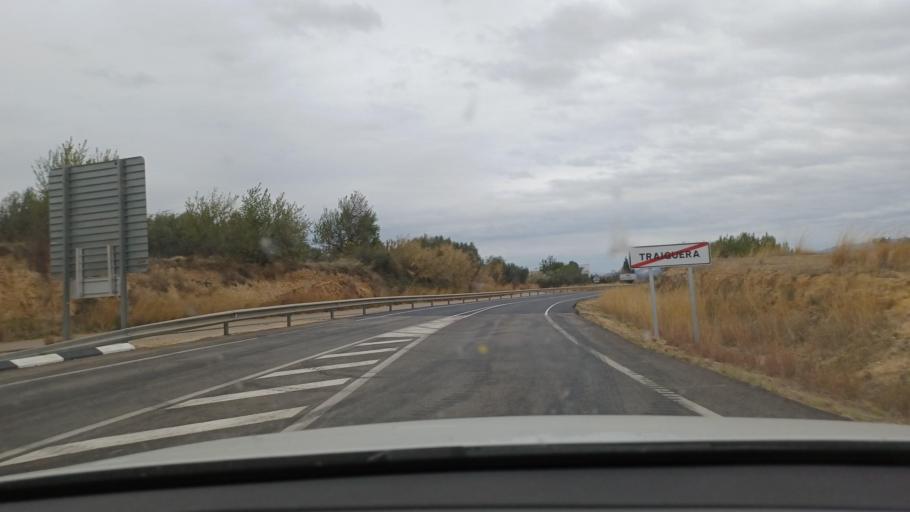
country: ES
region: Valencia
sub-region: Provincia de Castello
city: Traiguera
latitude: 40.5291
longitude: 0.2949
